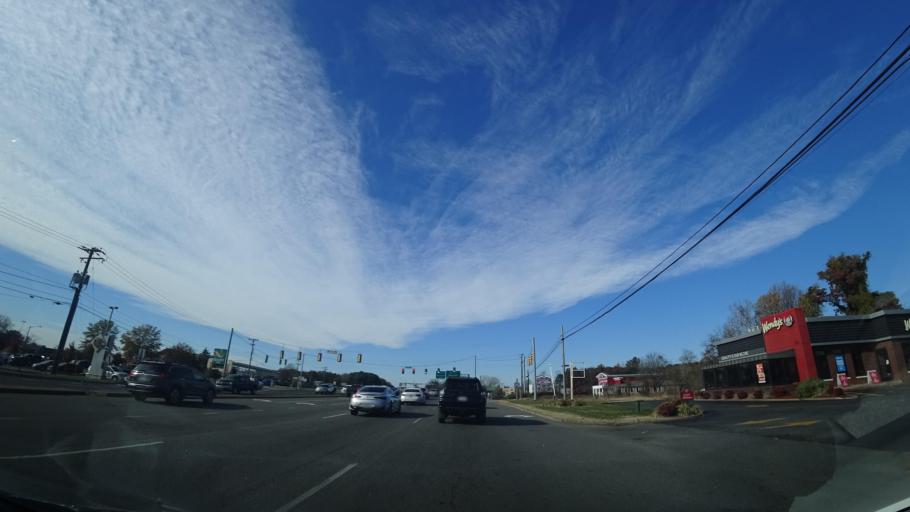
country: US
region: Virginia
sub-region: City of Fredericksburg
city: Fredericksburg
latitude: 38.2953
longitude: -77.4981
